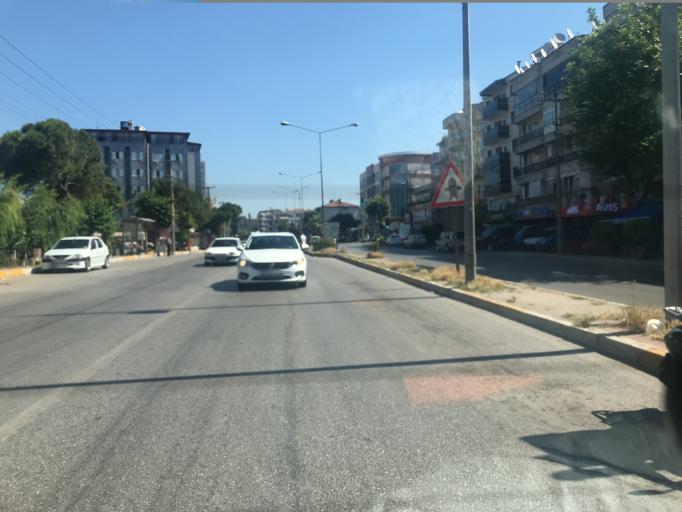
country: TR
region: Manisa
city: Akhisar
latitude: 38.9223
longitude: 27.8338
